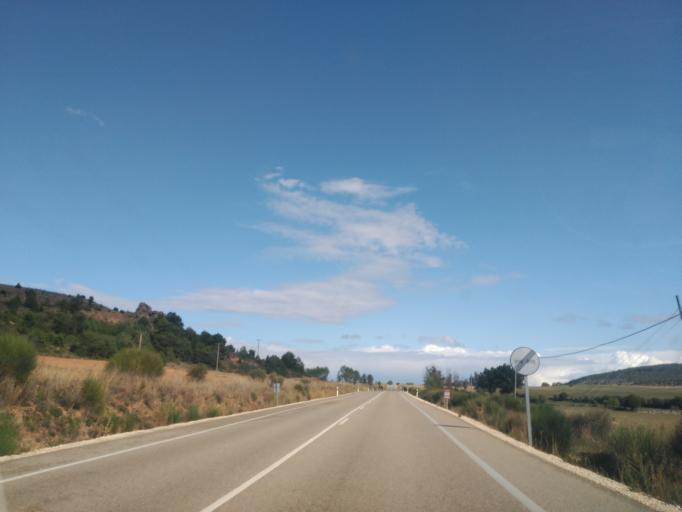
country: ES
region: Castille and Leon
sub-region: Provincia de Burgos
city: Hontoria del Pinar
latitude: 41.8550
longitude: -3.1889
